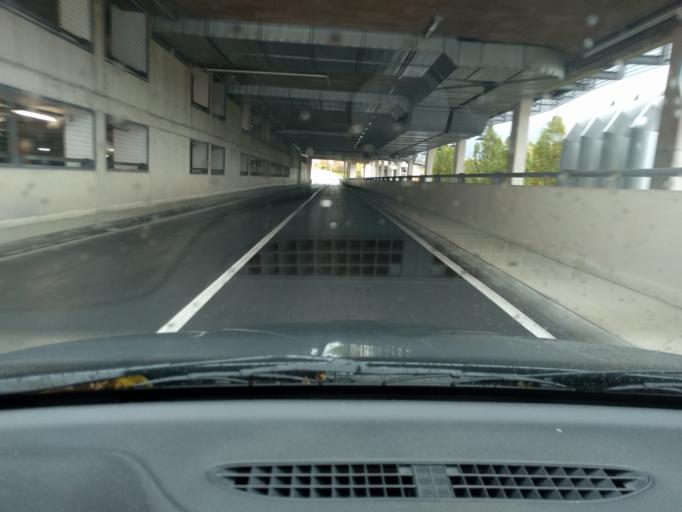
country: AT
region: Styria
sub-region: Politischer Bezirk Leoben
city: Leoben
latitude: 47.3824
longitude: 15.0964
